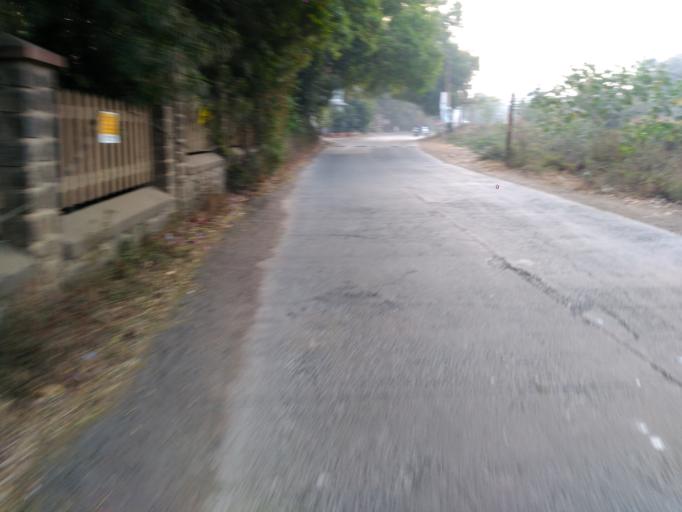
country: IN
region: Maharashtra
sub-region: Pune Division
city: Pune
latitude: 18.4615
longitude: 73.9069
